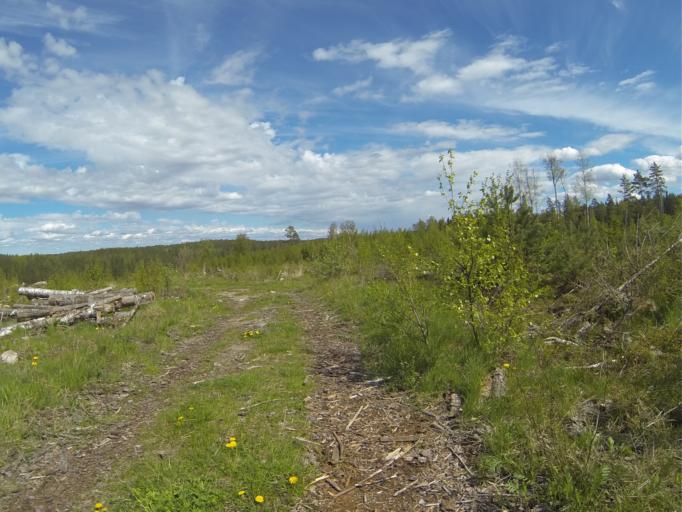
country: FI
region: Varsinais-Suomi
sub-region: Salo
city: Halikko
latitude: 60.3256
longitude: 23.0651
